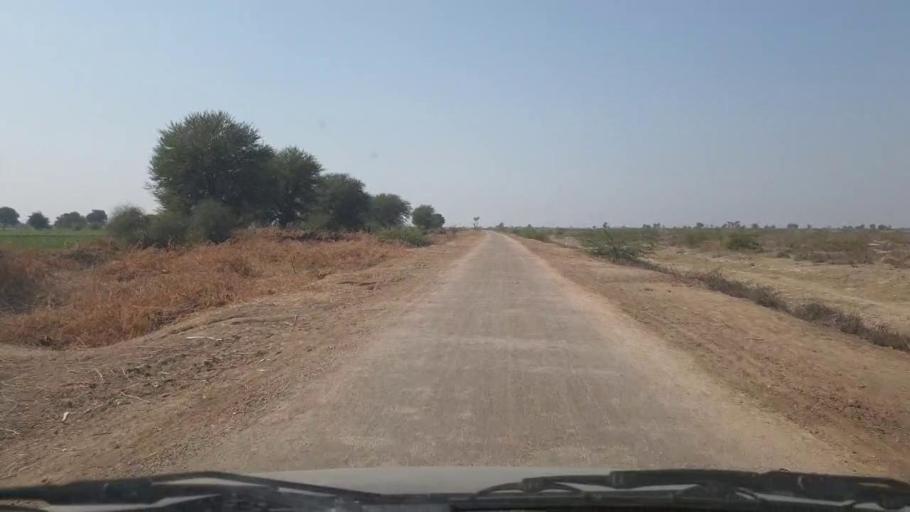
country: PK
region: Sindh
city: Samaro
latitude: 25.2601
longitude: 69.3338
